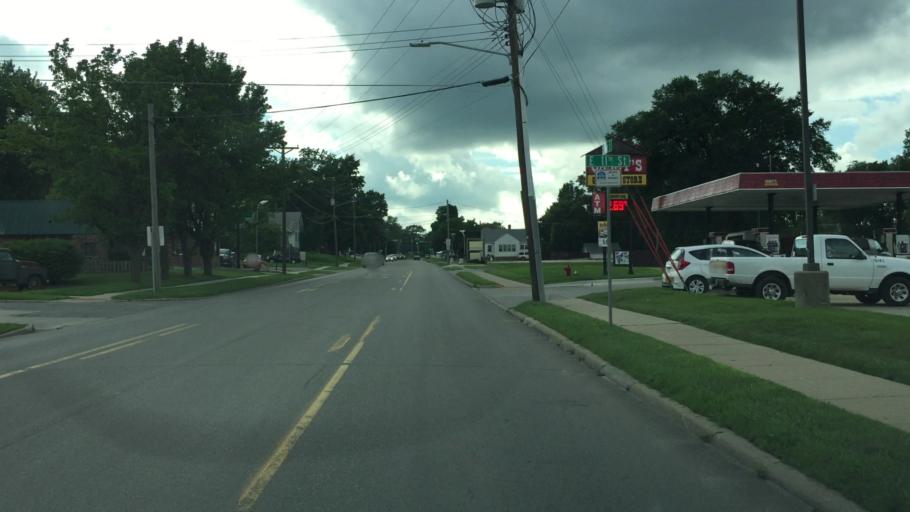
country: US
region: Iowa
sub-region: Jasper County
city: Newton
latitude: 41.6993
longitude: -93.0397
